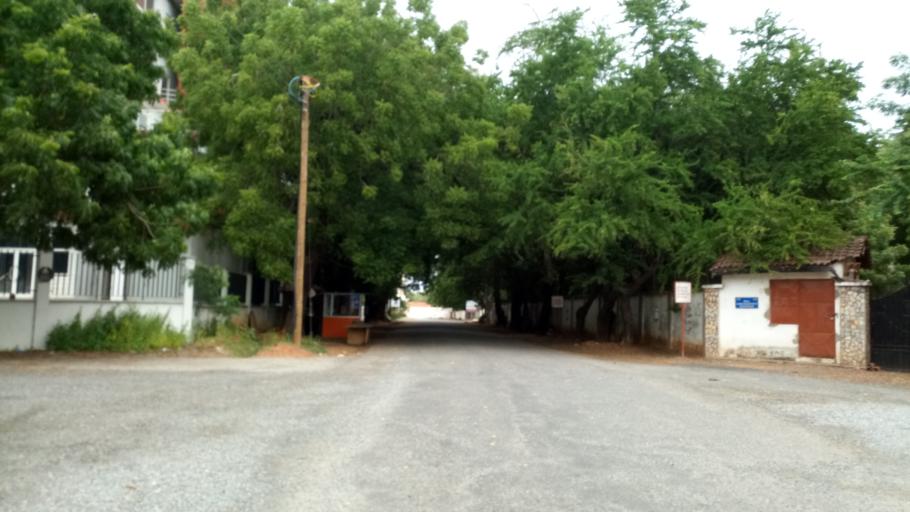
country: GH
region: Greater Accra
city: Accra
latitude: 5.5587
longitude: -0.1947
